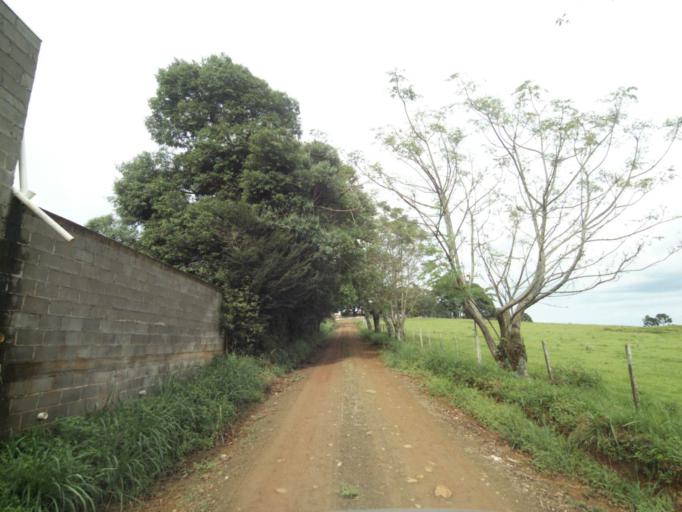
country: BR
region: Rio Grande do Sul
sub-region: Lagoa Vermelha
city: Lagoa Vermelha
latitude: -28.2292
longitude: -51.5075
